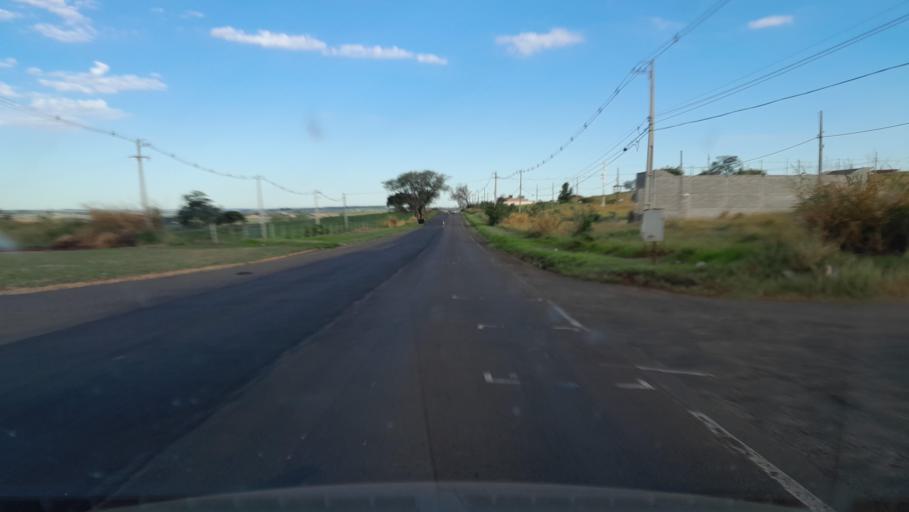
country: BR
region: Parana
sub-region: Umuarama
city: Umuarama
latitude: -23.7640
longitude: -53.2704
